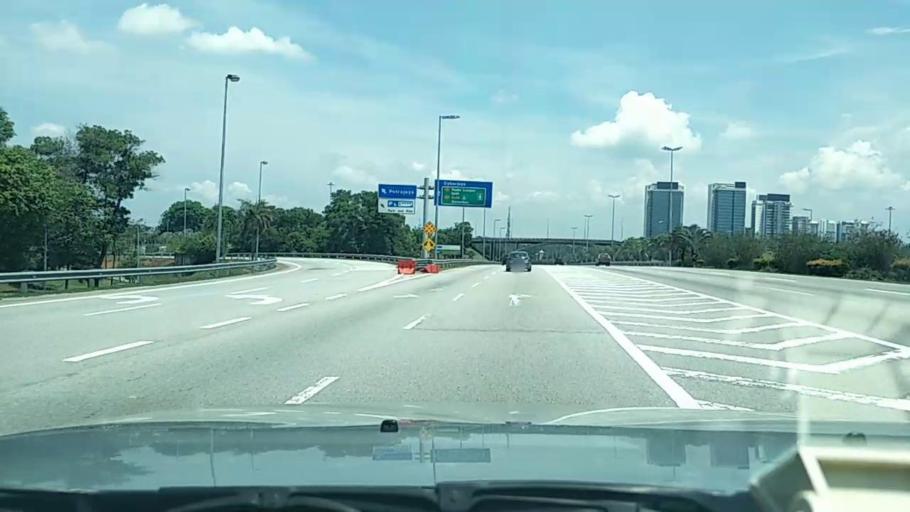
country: MY
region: Putrajaya
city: Putrajaya
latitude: 2.9319
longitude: 101.6673
